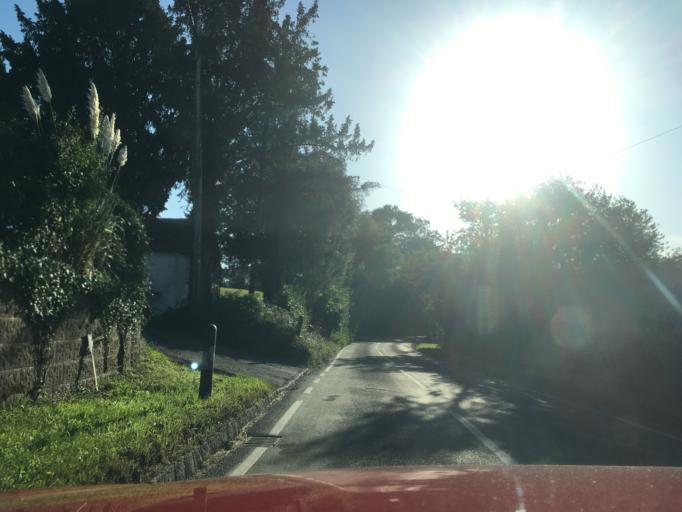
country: GB
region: England
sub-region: Hampshire
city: Bishops Waltham
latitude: 50.9353
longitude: -1.2086
